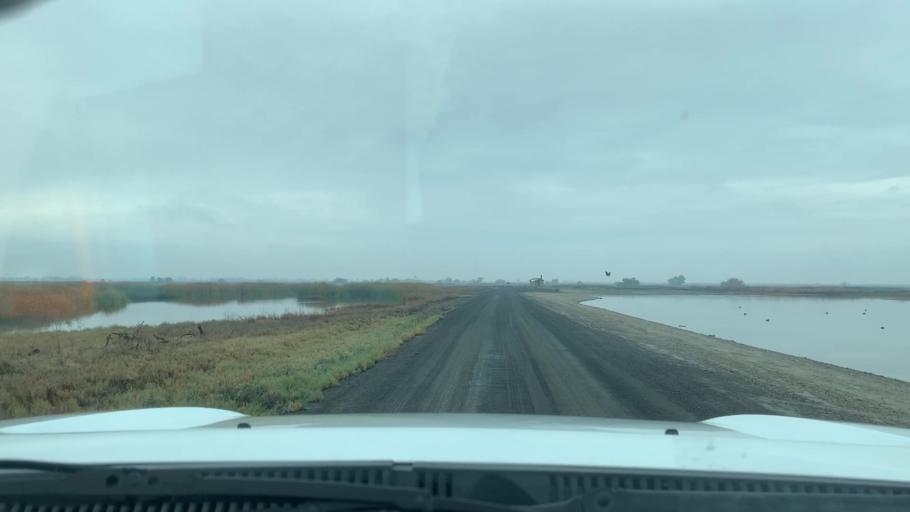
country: US
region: California
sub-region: Kern County
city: Lost Hills
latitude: 35.7336
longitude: -119.6065
